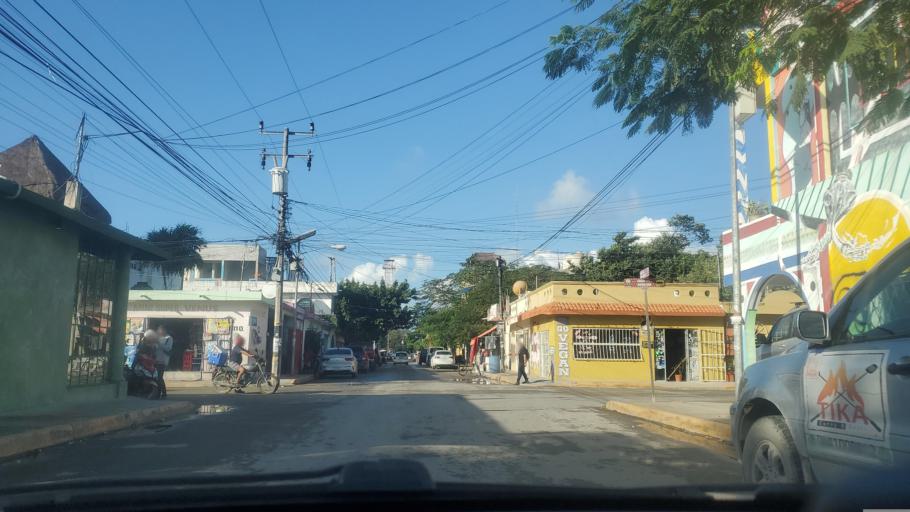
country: MX
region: Quintana Roo
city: Tulum
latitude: 20.2105
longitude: -87.4600
